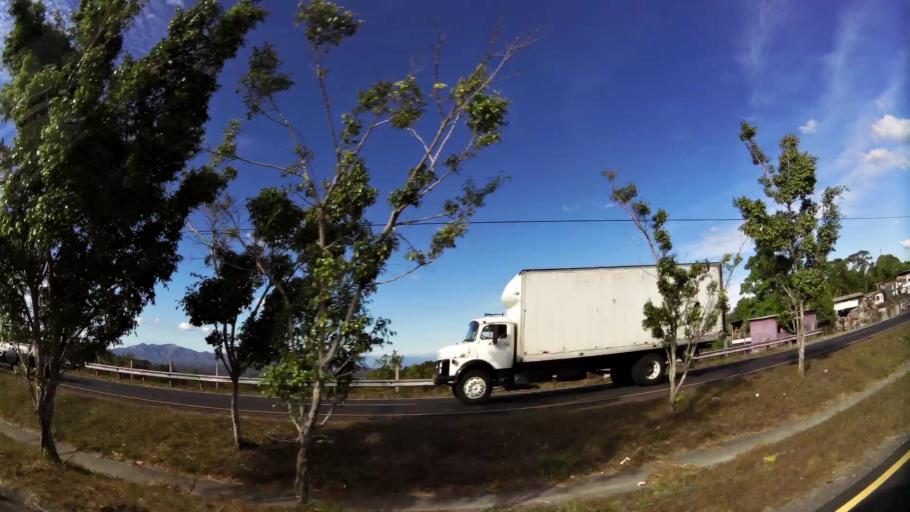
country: SV
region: Cuscatlan
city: Tecoluca
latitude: 13.7466
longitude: -89.0296
